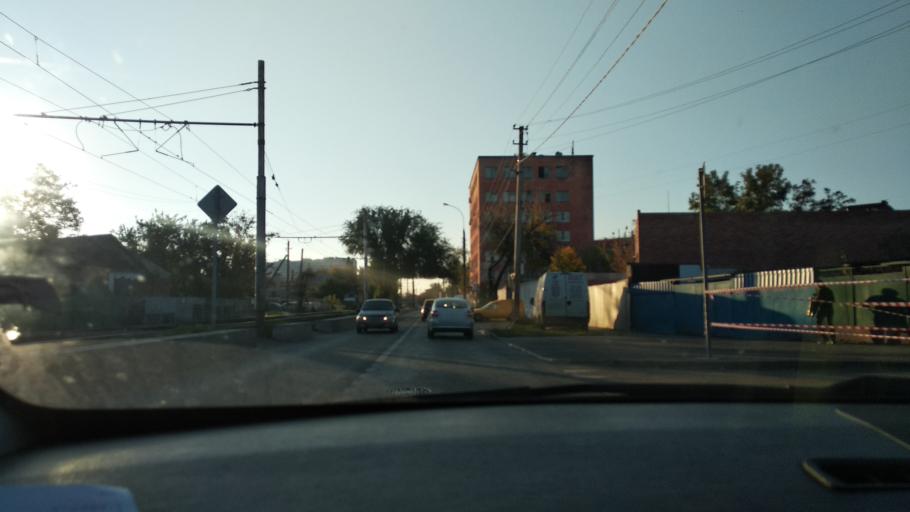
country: RU
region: Krasnodarskiy
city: Krasnodar
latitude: 45.0093
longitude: 39.0141
